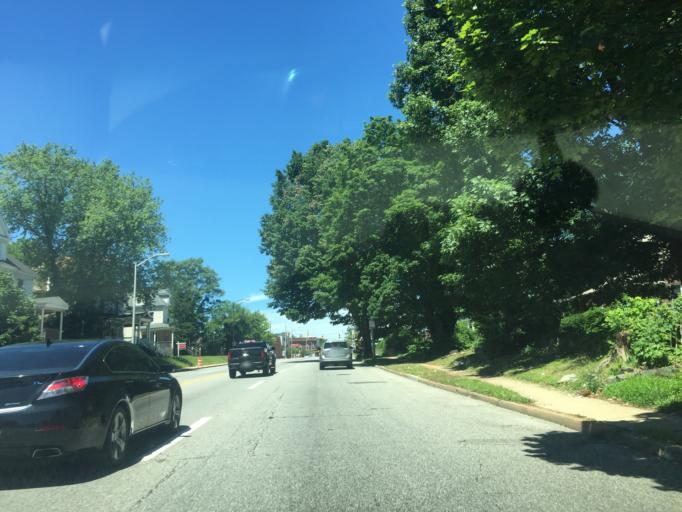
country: US
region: Maryland
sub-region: Baltimore County
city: Lochearn
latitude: 39.3265
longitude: -76.6795
